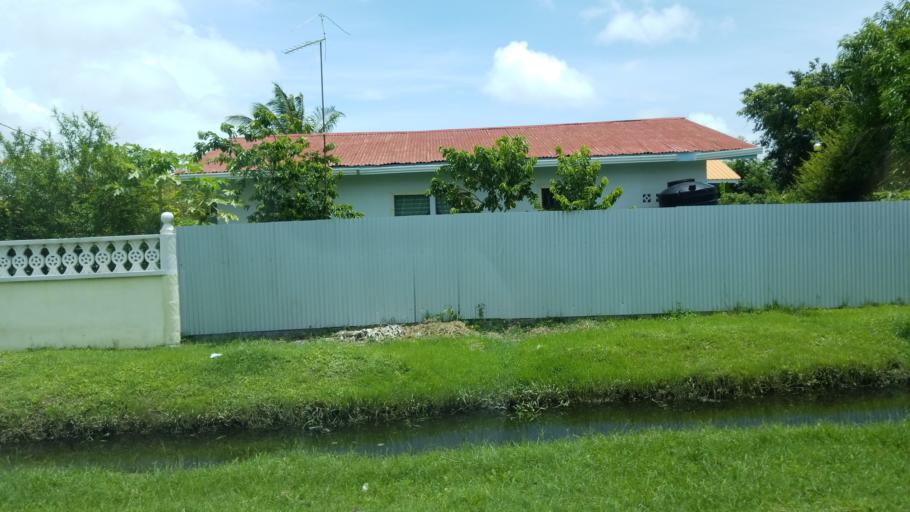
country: GY
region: Demerara-Mahaica
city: Georgetown
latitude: 6.7930
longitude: -58.1202
